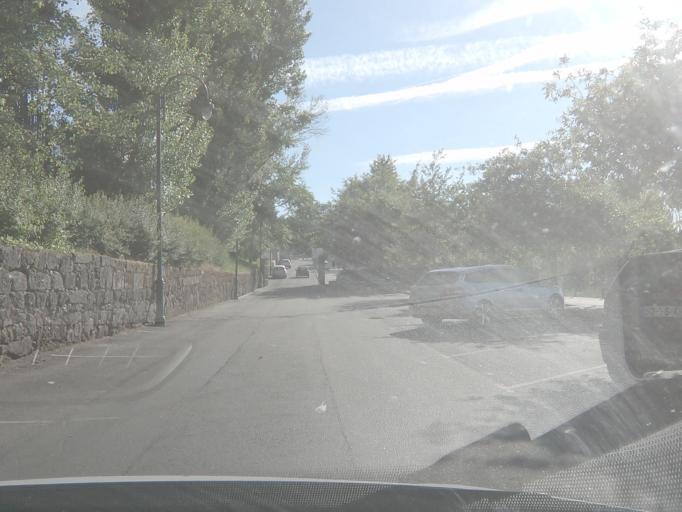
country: PT
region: Viseu
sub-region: Viseu
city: Viseu
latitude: 40.6605
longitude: -7.9033
